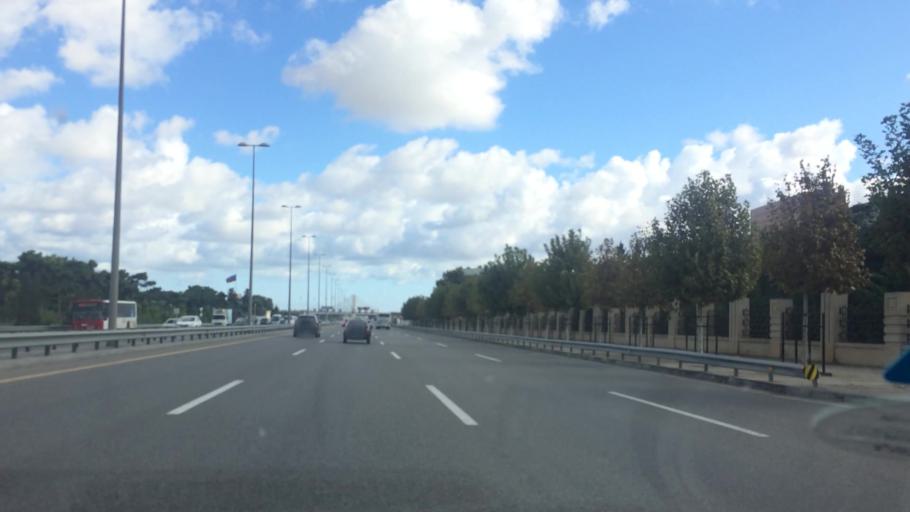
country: AZ
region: Baki
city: Biny Selo
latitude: 40.4540
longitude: 50.0660
